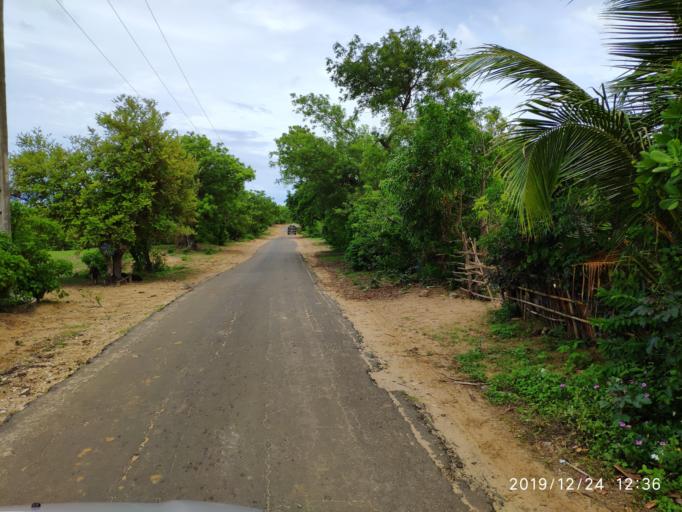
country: MG
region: Diana
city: Antsiranana
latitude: -12.3095
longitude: 49.3483
